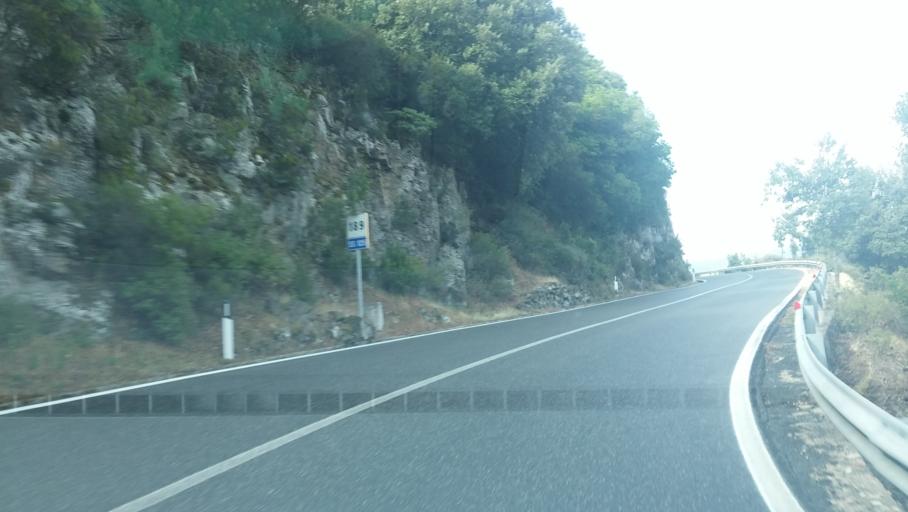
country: IT
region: Sardinia
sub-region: Provincia di Ogliastra
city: Urzulei
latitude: 40.1857
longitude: 9.5359
